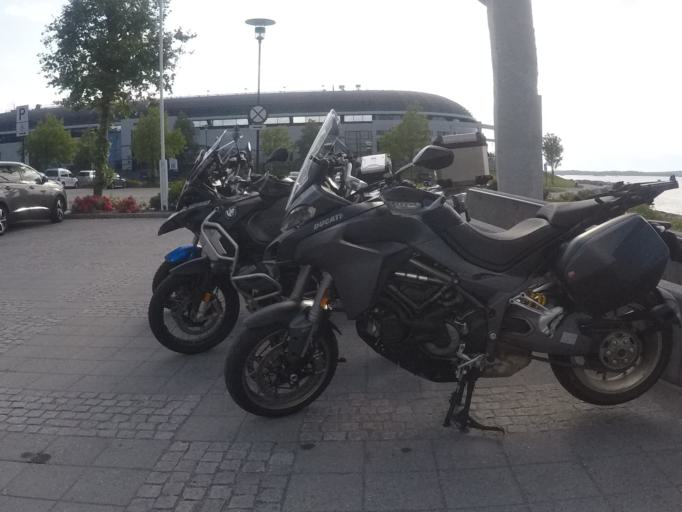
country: NO
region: More og Romsdal
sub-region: Molde
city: Molde
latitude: 62.7331
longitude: 7.1445
